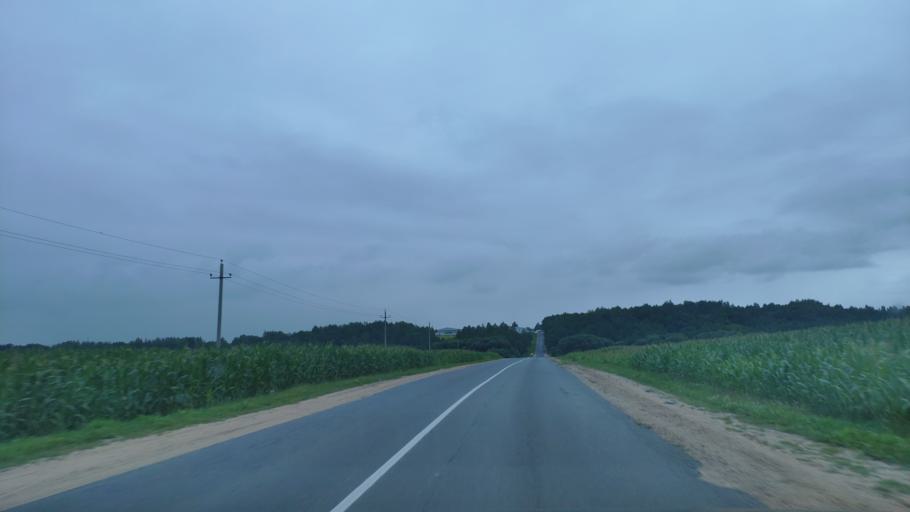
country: BY
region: Minsk
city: Azyartso
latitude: 53.8374
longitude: 27.3584
